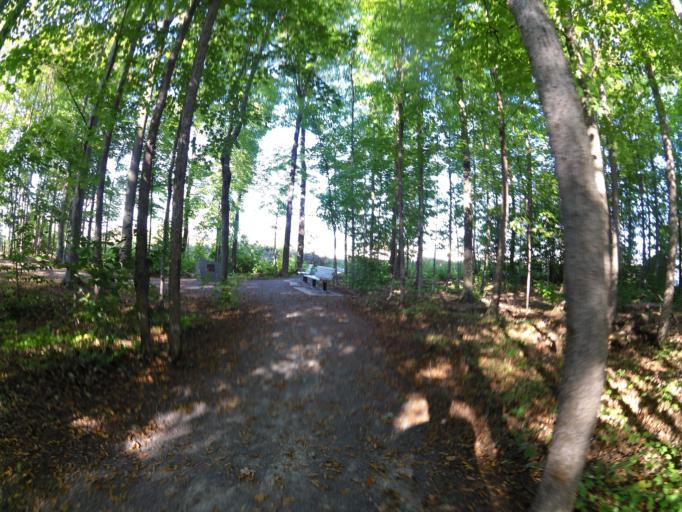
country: CA
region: Ontario
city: Bells Corners
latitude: 45.3501
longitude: -75.9500
